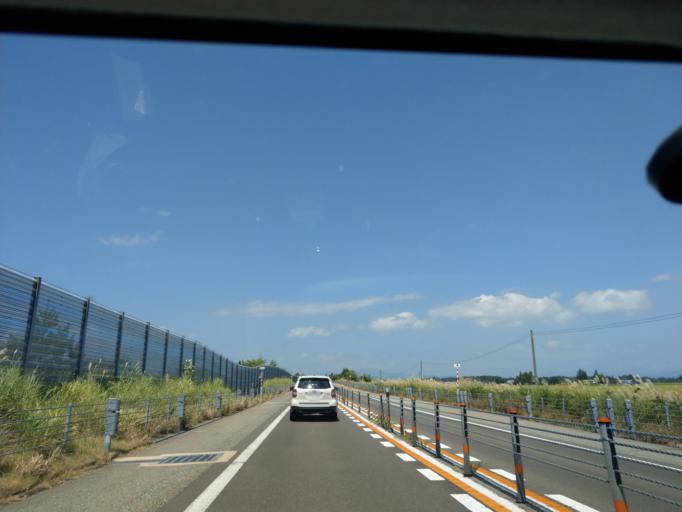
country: JP
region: Akita
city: Omagari
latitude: 39.3861
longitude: 140.4789
